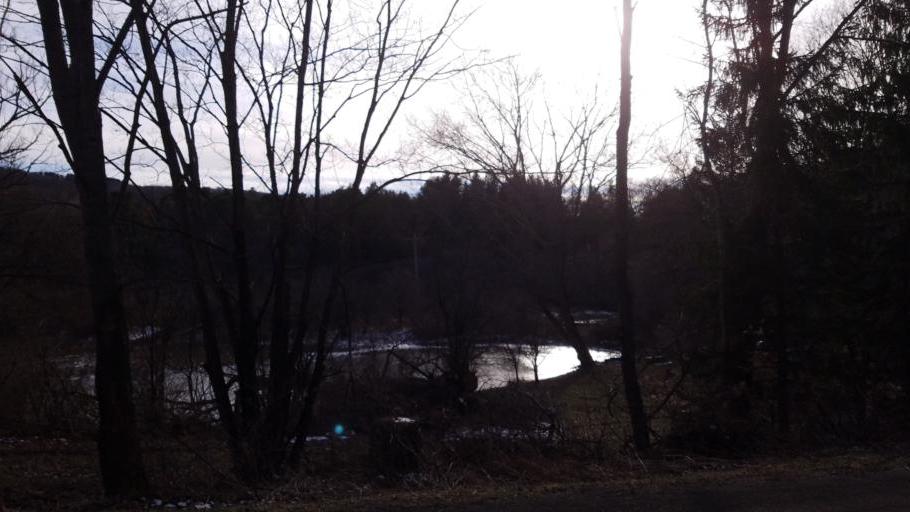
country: US
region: New York
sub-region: Allegany County
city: Wellsville
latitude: 42.1717
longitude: -77.9349
